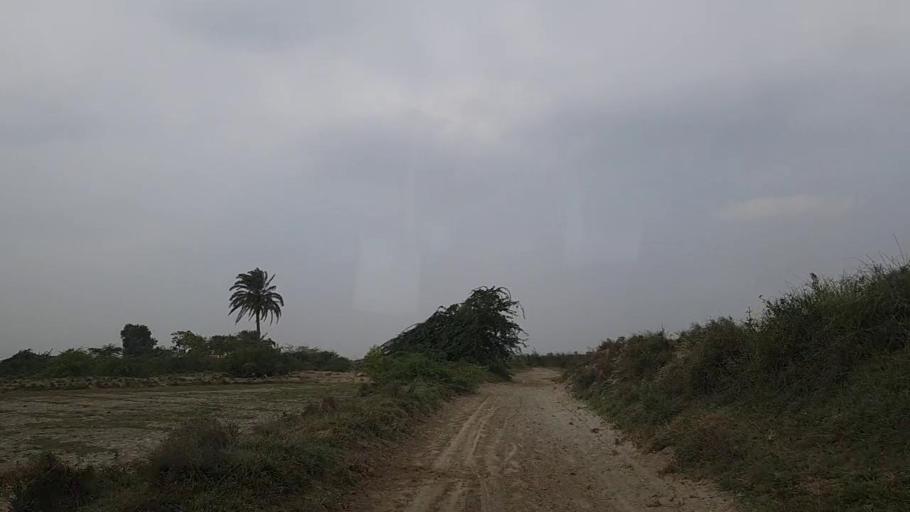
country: PK
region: Sindh
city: Mirpur Sakro
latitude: 24.5955
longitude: 67.6973
